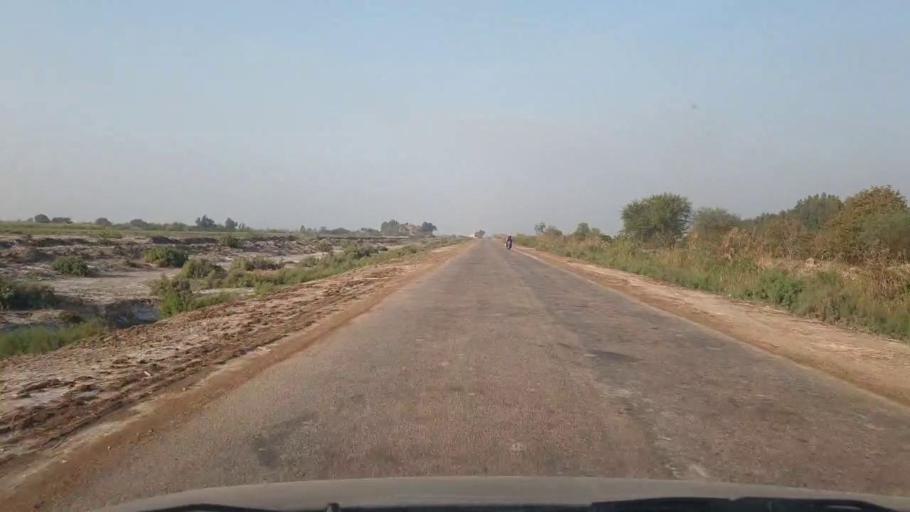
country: PK
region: Sindh
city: Mirwah Gorchani
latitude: 25.3420
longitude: 69.1699
